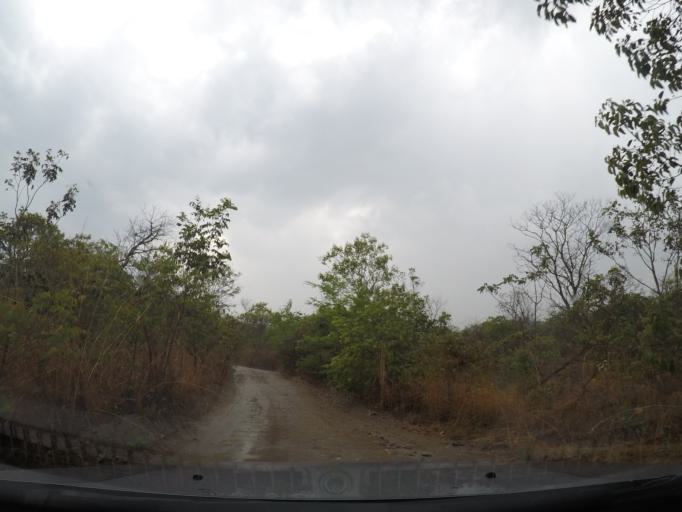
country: BR
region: Goias
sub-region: Pirenopolis
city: Pirenopolis
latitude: -15.8278
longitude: -48.8840
